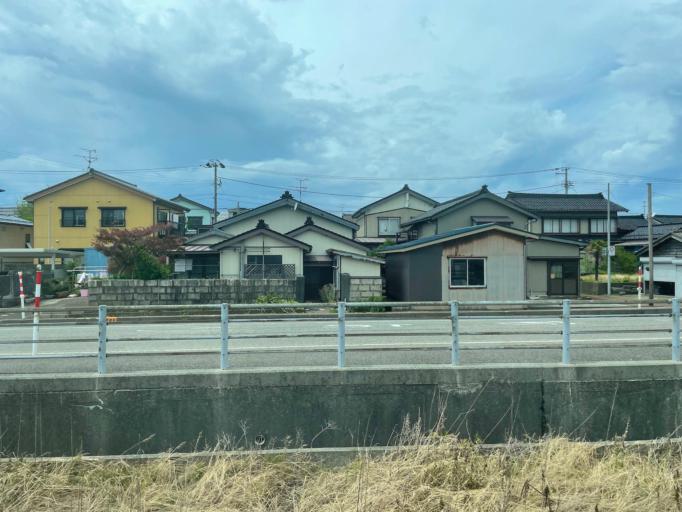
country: JP
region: Niigata
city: Itoigawa
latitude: 37.0536
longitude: 137.8971
